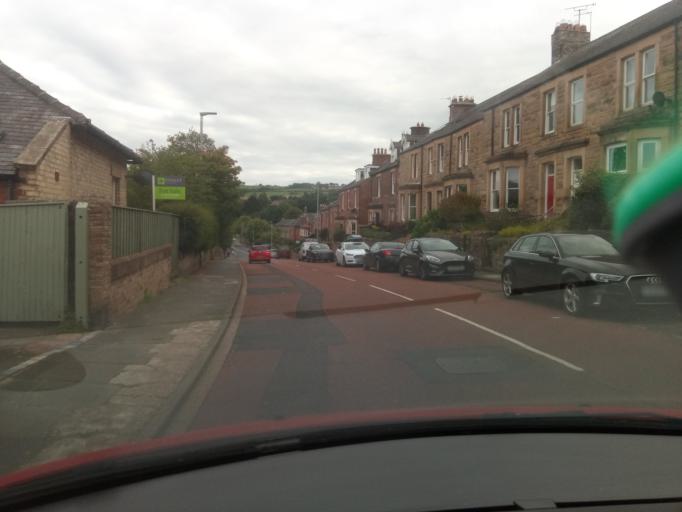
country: GB
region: England
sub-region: Northumberland
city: Hexham
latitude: 54.9729
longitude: -2.1133
